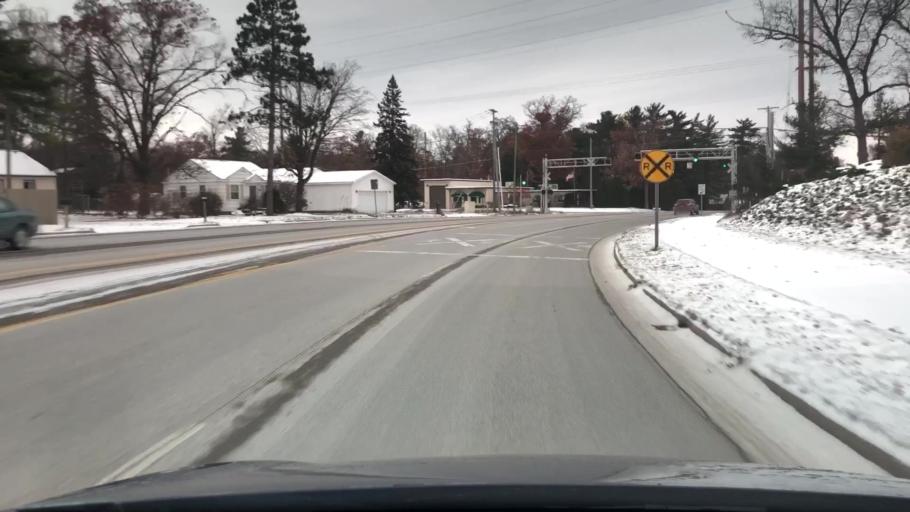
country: US
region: Michigan
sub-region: Grand Traverse County
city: Traverse City
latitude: 44.7449
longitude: -85.5610
